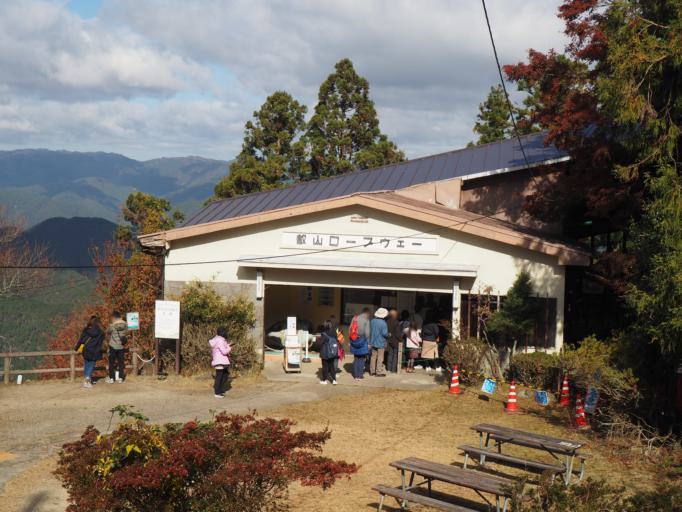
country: JP
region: Kyoto
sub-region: Kyoto-shi
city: Kamigyo-ku
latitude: 35.0646
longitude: 135.8224
